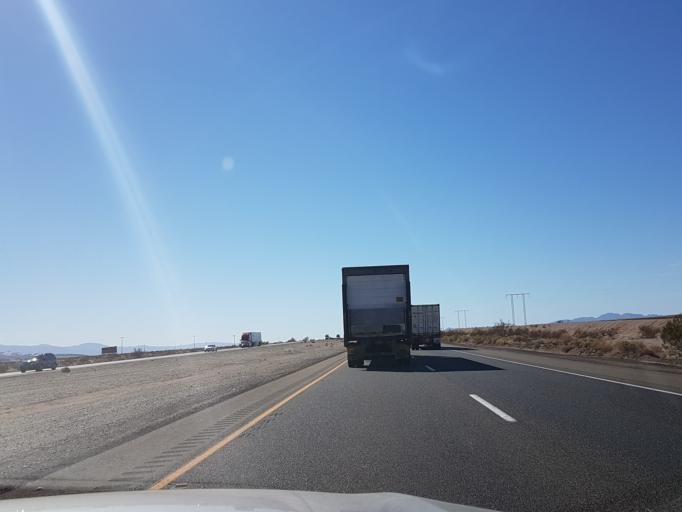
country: US
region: California
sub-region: San Bernardino County
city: Fort Irwin
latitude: 35.0288
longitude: -116.4821
